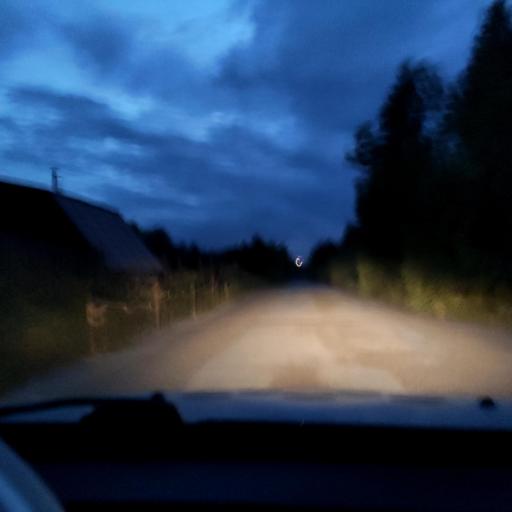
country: RU
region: Perm
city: Kondratovo
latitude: 58.0295
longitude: 56.0650
